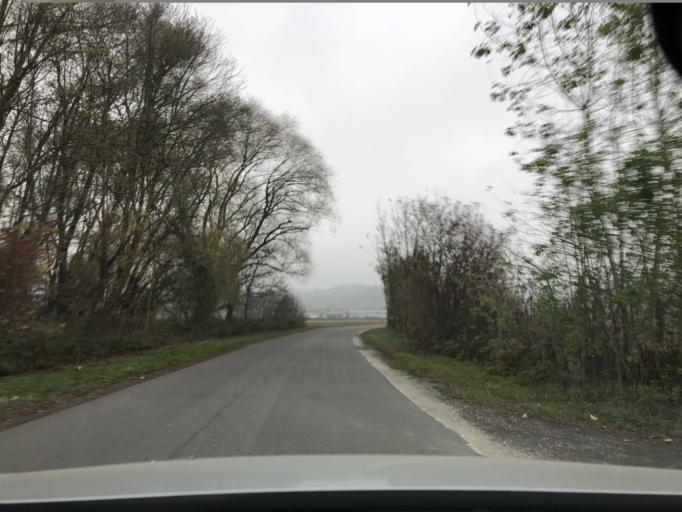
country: AT
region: Styria
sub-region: Politischer Bezirk Suedoststeiermark
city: Fehring
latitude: 46.9442
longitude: 16.0313
